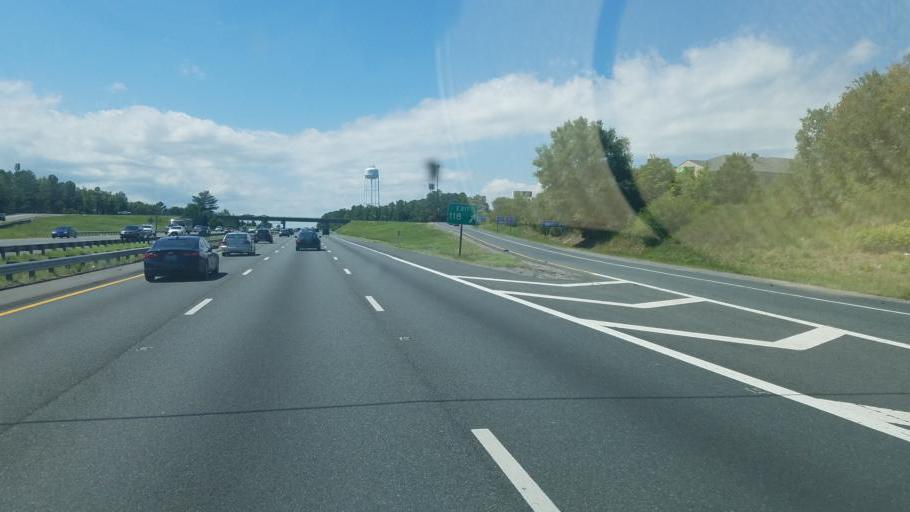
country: US
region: Virginia
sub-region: Spotsylvania County
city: Spotsylvania Courthouse
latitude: 38.1356
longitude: -77.5098
